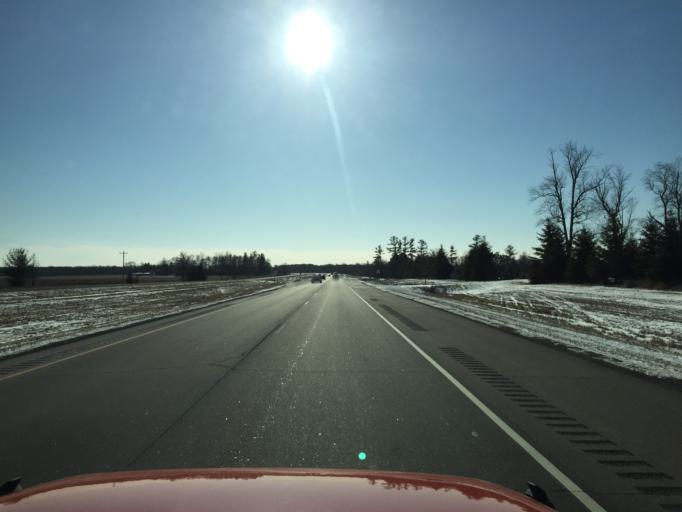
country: US
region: Minnesota
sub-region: Mille Lacs County
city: Milaca
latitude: 45.8393
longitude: -93.6617
